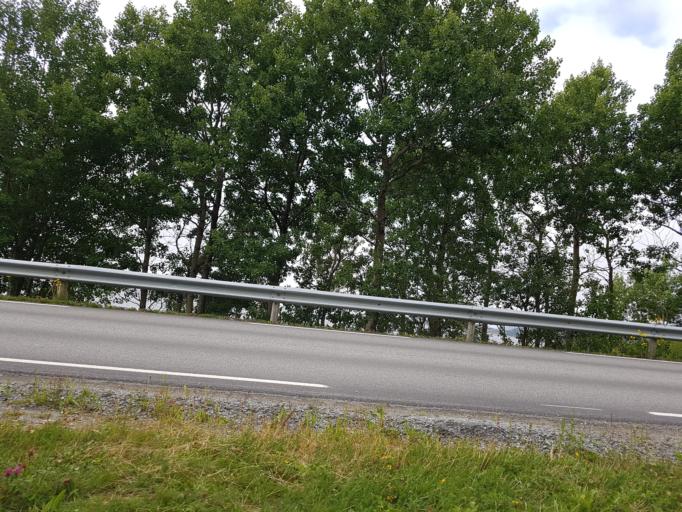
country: NO
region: Sor-Trondelag
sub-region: Agdenes
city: Lensvik
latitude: 63.6345
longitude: 9.8319
